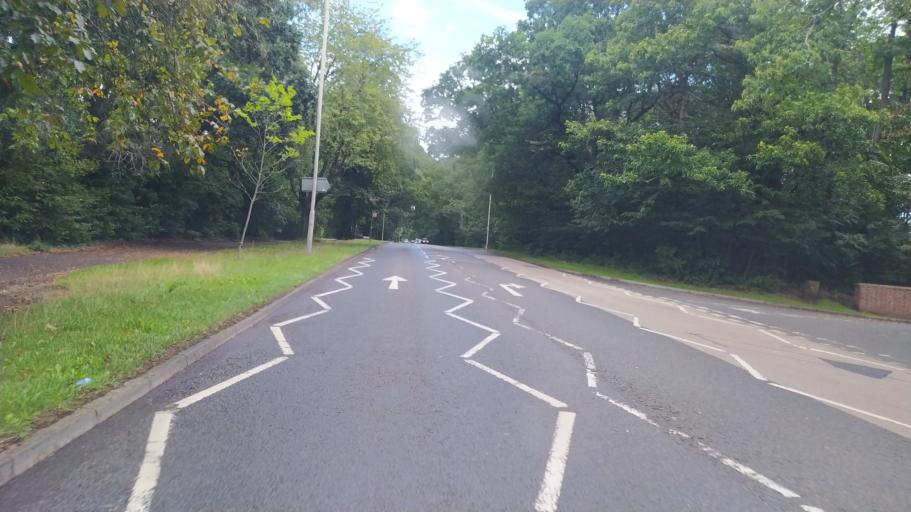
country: GB
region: England
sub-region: Dorset
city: Broadstone
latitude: 50.7550
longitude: -1.9819
